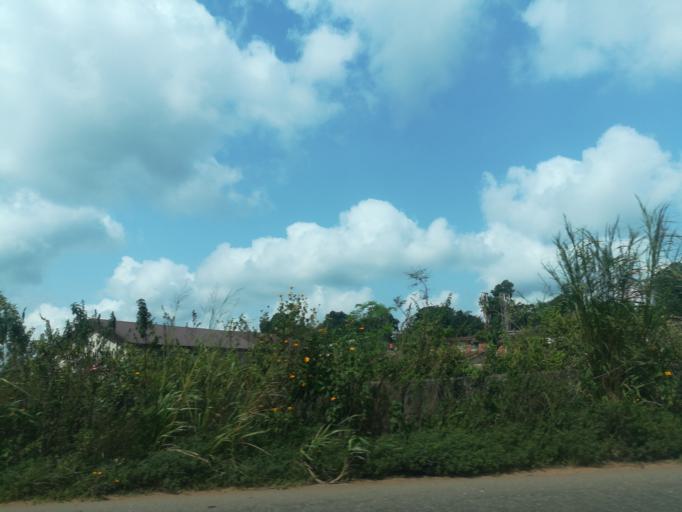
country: NG
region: Oyo
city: Moniya
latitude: 7.4918
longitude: 3.9163
